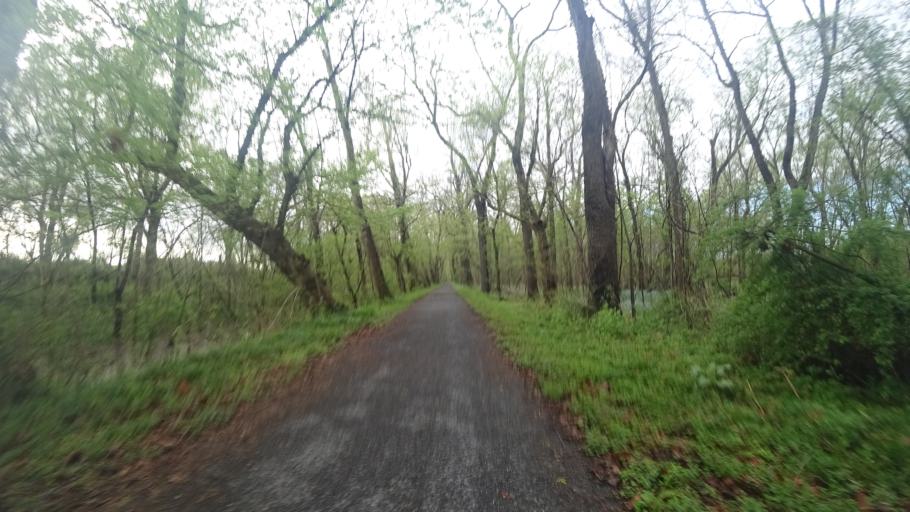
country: US
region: Virginia
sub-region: Loudoun County
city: Leesburg
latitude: 39.1433
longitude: -77.5171
